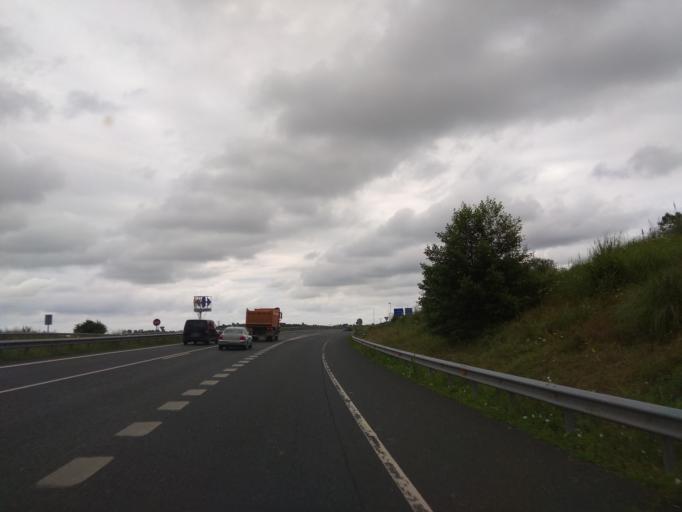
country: ES
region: Cantabria
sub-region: Provincia de Cantabria
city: Torrelavega
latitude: 43.3386
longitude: -4.0314
